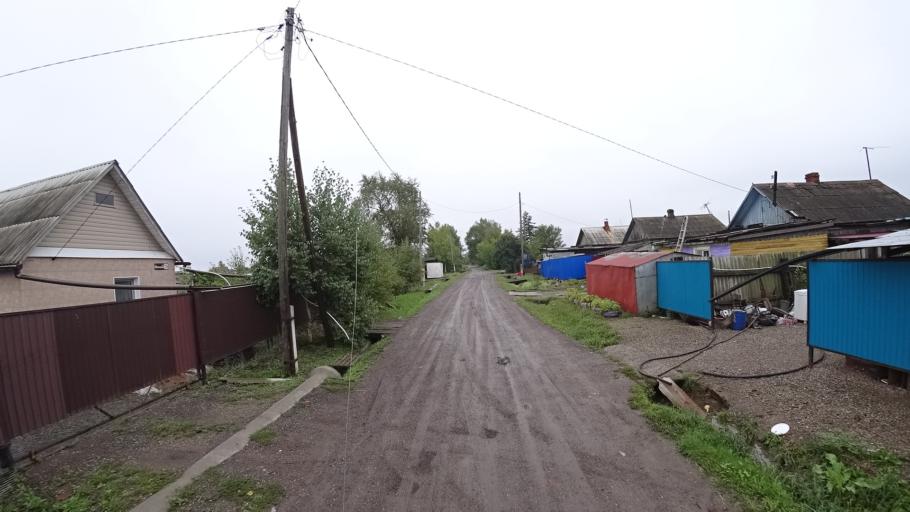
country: RU
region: Primorskiy
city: Monastyrishche
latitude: 44.2023
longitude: 132.4200
